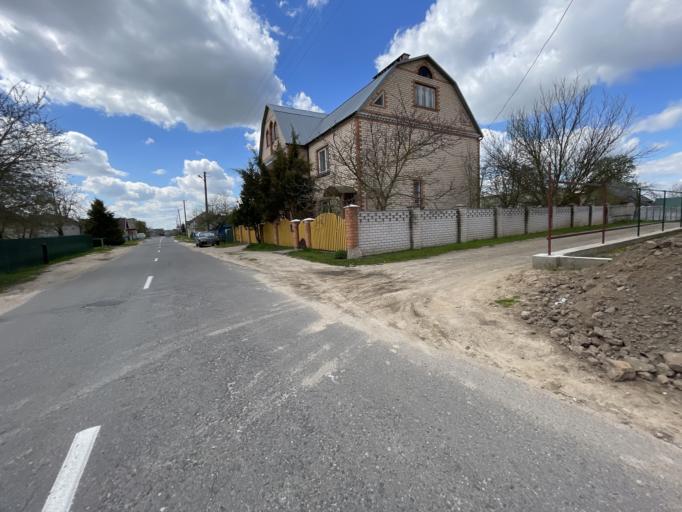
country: BY
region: Minsk
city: Nyasvizh
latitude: 53.2091
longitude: 26.6843
